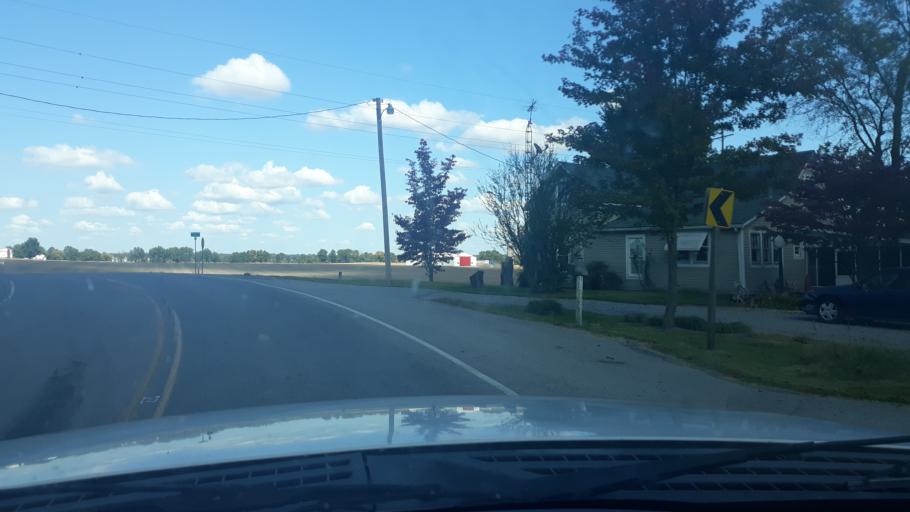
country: US
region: Illinois
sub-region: Saline County
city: Eldorado
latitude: 37.7895
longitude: -88.4850
